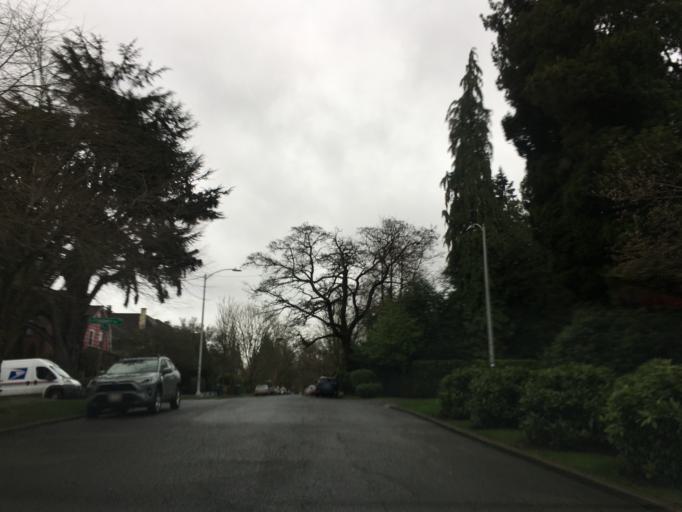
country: US
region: Washington
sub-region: King County
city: Seattle
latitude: 47.6290
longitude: -122.3100
